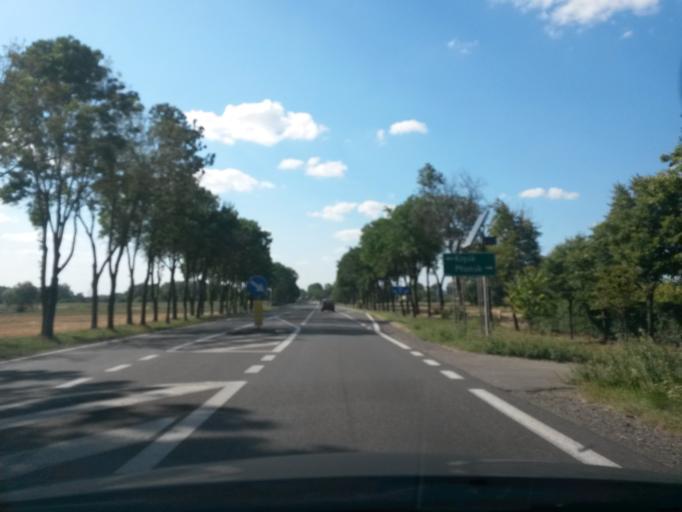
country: PL
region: Masovian Voivodeship
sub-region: Powiat plonski
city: Plonsk
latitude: 52.6077
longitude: 20.3826
